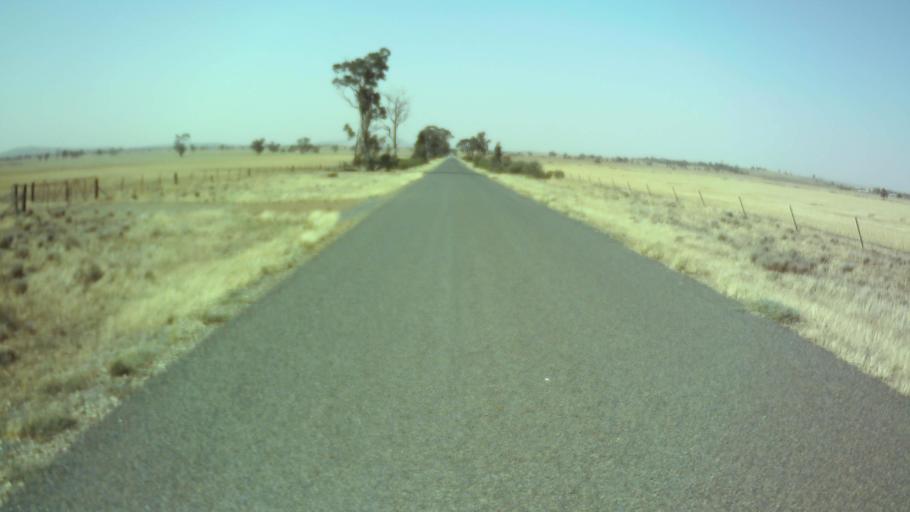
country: AU
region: New South Wales
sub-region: Weddin
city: Grenfell
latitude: -33.8804
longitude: 147.9245
